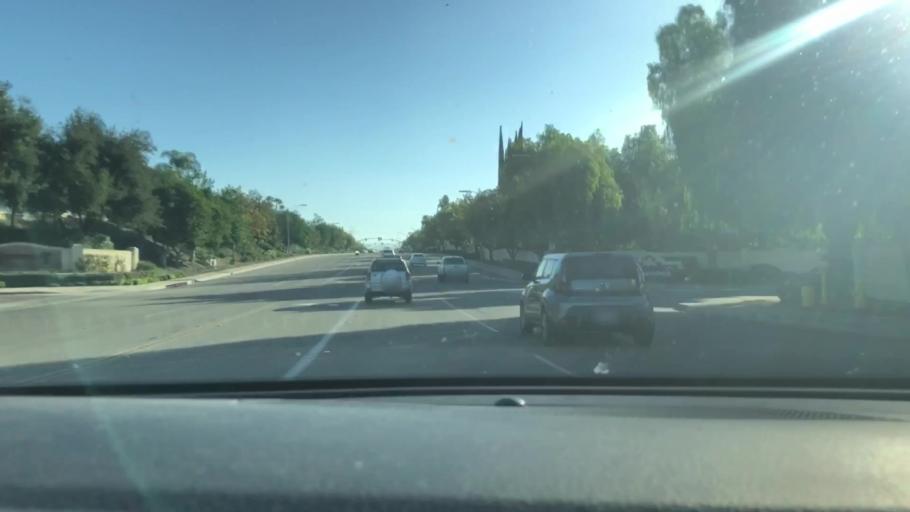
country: US
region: California
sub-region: Riverside County
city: Murrieta
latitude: 33.5956
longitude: -117.1941
